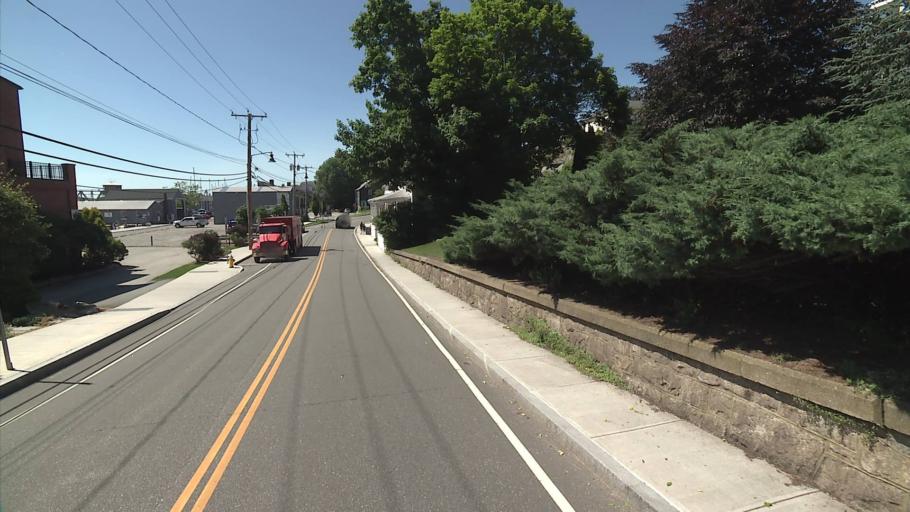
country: US
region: Connecticut
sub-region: New London County
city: Mystic
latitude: 41.3525
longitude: -71.9723
